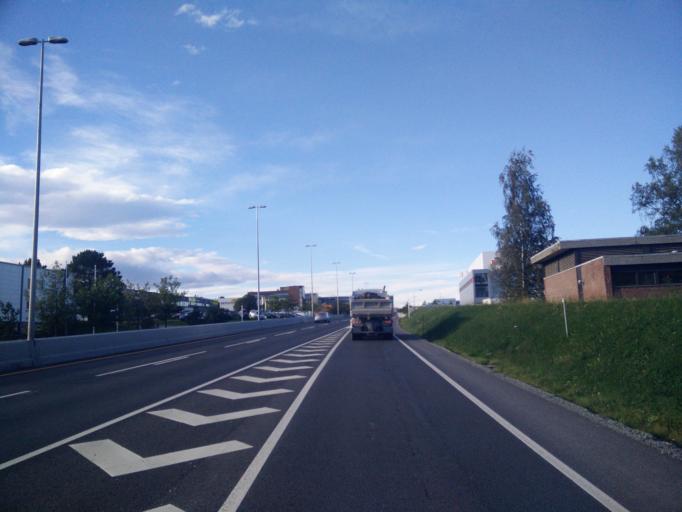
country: NO
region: Sor-Trondelag
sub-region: Trondheim
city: Trondheim
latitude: 63.4249
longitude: 10.4737
